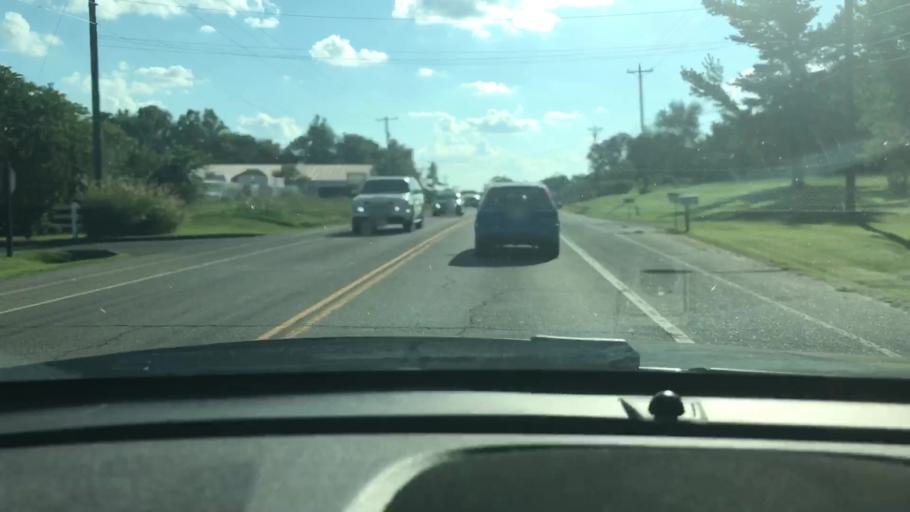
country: US
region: Tennessee
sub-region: Sumner County
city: White House
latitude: 36.4637
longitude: -86.6601
